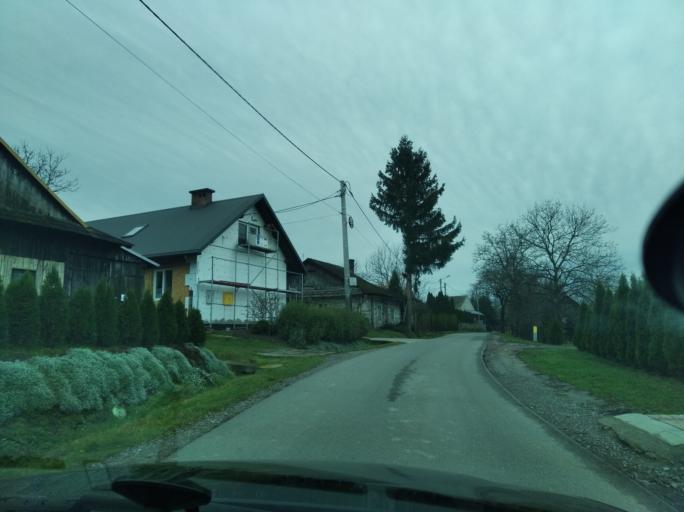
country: PL
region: Subcarpathian Voivodeship
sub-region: Powiat lancucki
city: Markowa
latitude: 50.0239
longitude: 22.3321
